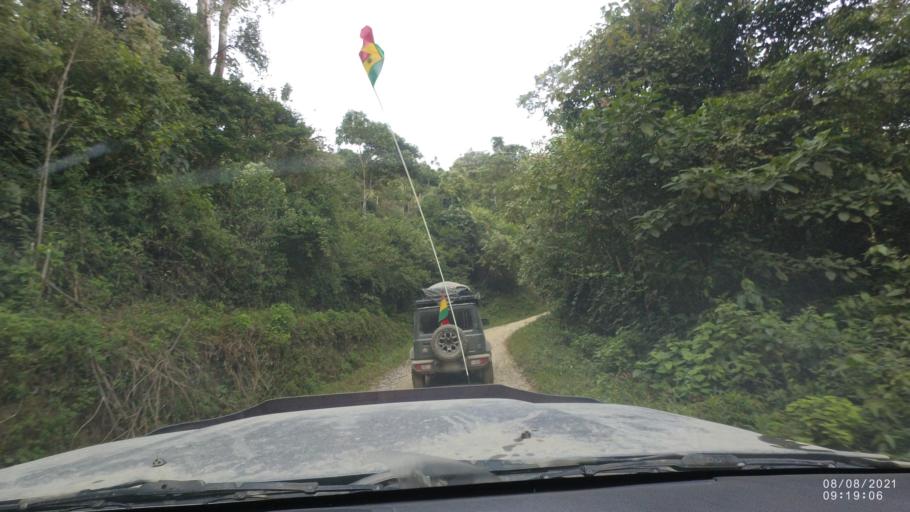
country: BO
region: La Paz
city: Quime
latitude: -16.5701
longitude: -66.7167
